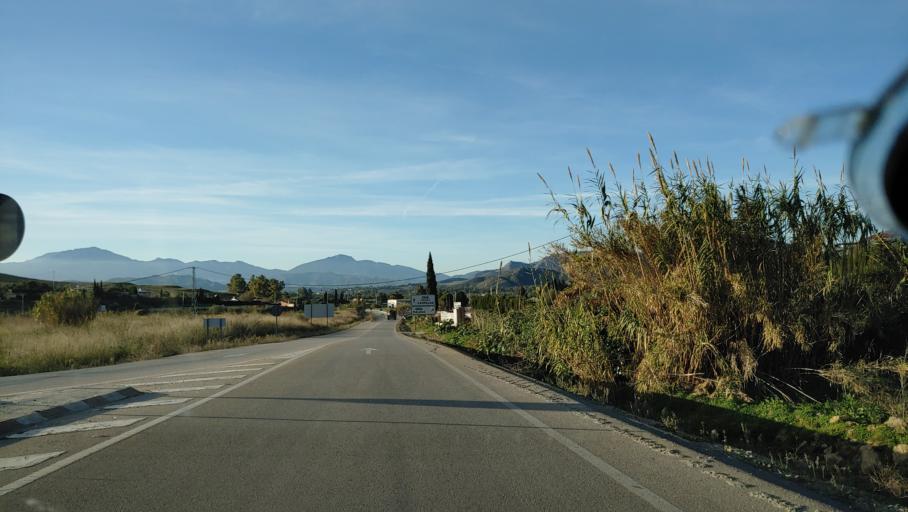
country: ES
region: Andalusia
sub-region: Provincia de Malaga
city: Cartama
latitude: 36.7125
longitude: -4.6424
